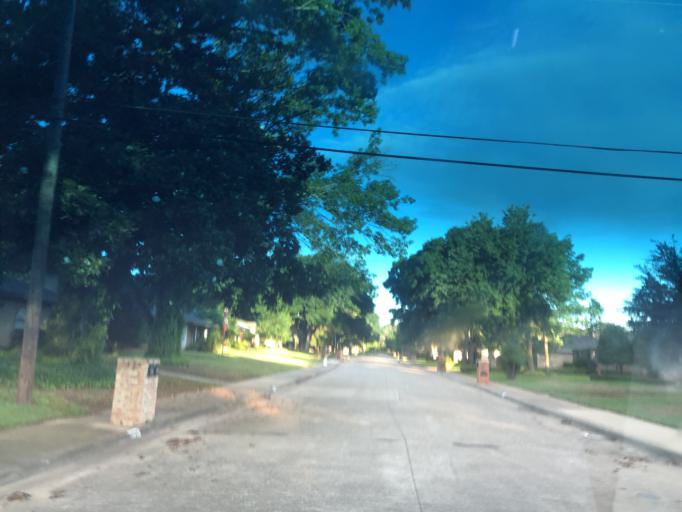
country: US
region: Texas
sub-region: Dallas County
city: Grand Prairie
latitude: 32.7817
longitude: -97.0334
